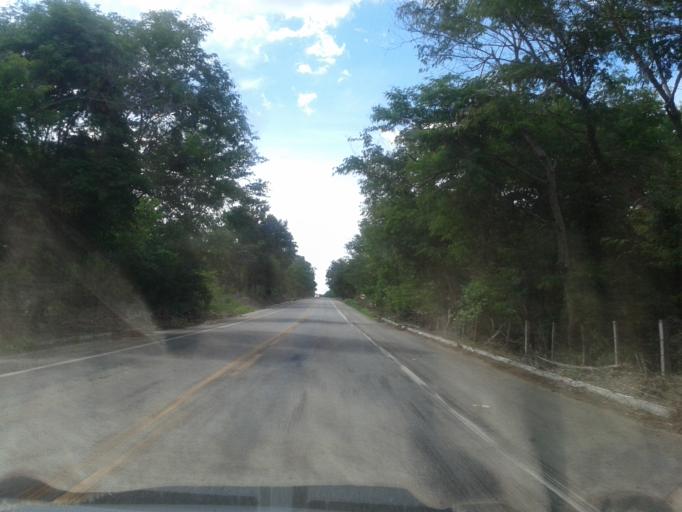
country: BR
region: Goias
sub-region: Itapuranga
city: Itapuranga
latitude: -15.4793
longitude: -50.3345
